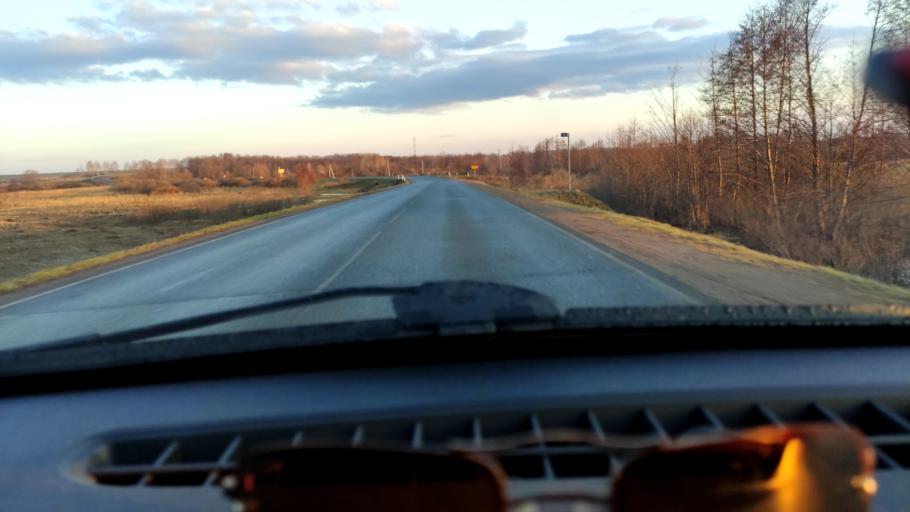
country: RU
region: Bashkortostan
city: Kabakovo
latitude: 54.5065
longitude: 56.1716
